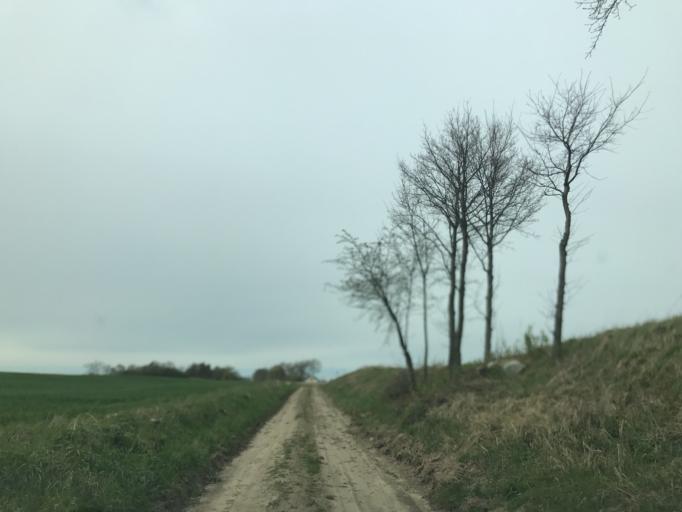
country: PL
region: Warmian-Masurian Voivodeship
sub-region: Powiat ilawski
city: Lubawa
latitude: 53.4156
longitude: 19.8129
